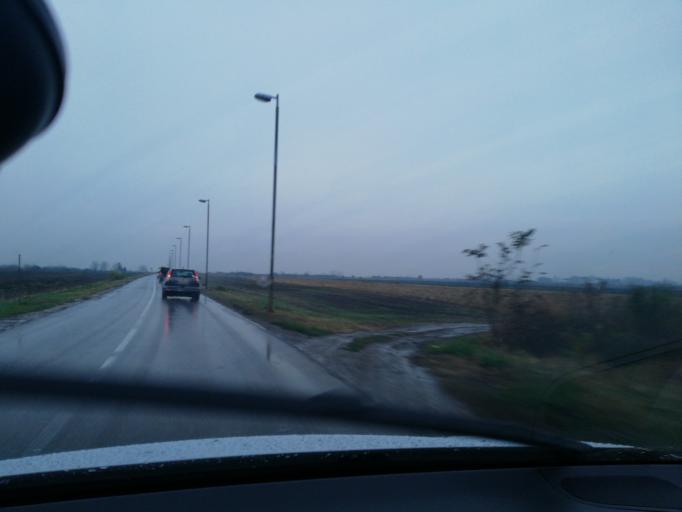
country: RS
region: Autonomna Pokrajina Vojvodina
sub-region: Sremski Okrug
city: Ruma
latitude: 44.9880
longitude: 19.8165
